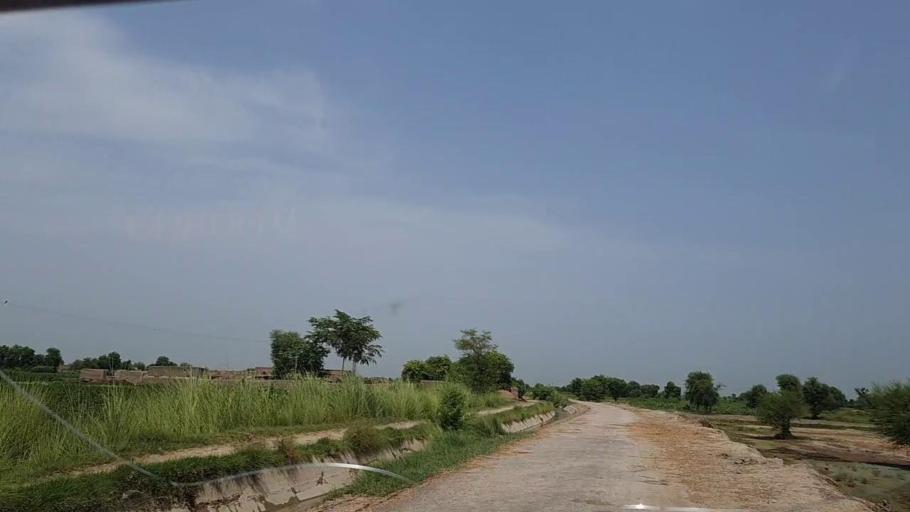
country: PK
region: Sindh
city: Tharu Shah
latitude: 26.9271
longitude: 68.0681
